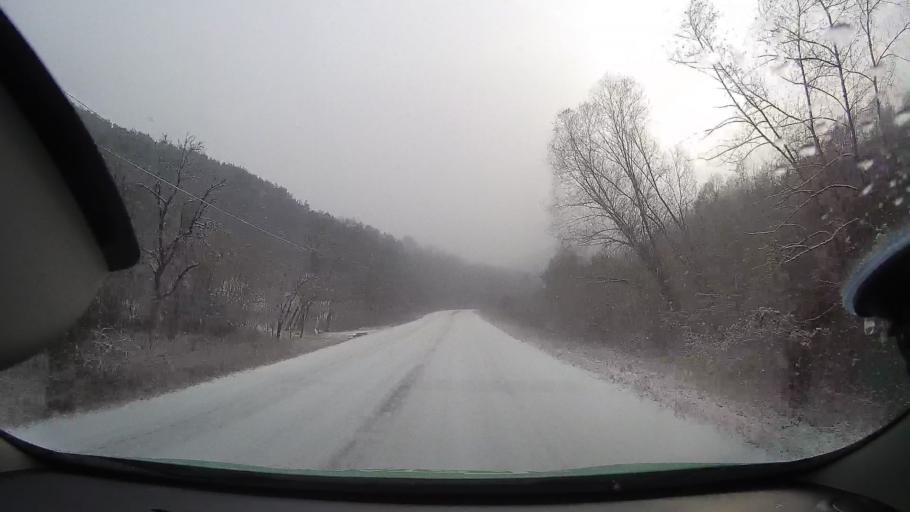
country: RO
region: Alba
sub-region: Comuna Livezile
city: Livezile
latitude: 46.3550
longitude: 23.6170
